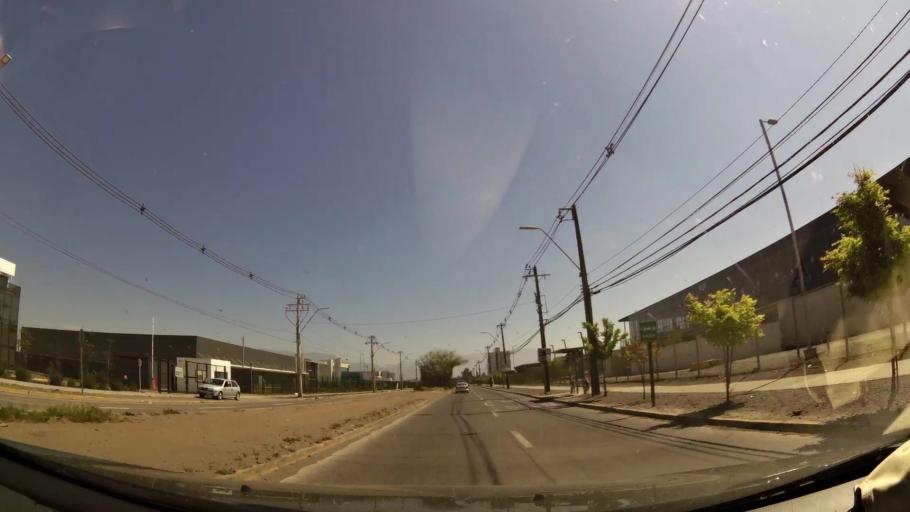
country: CL
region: Santiago Metropolitan
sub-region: Provincia de Santiago
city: Lo Prado
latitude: -33.3965
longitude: -70.7637
